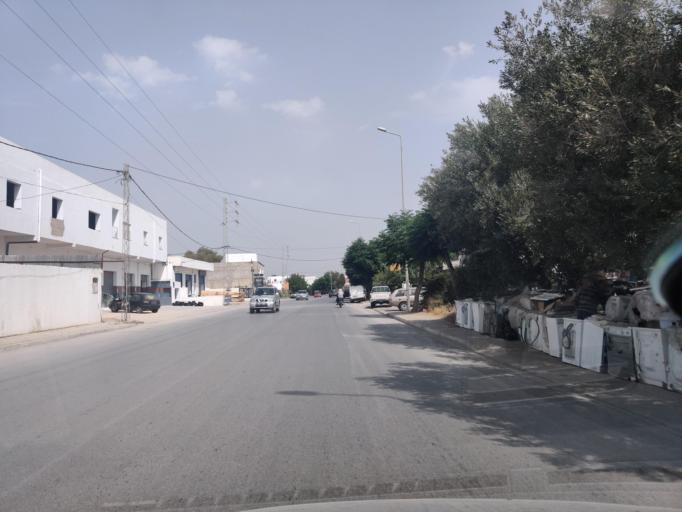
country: TN
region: Nabul
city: Al Hammamat
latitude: 36.4134
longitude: 10.5973
